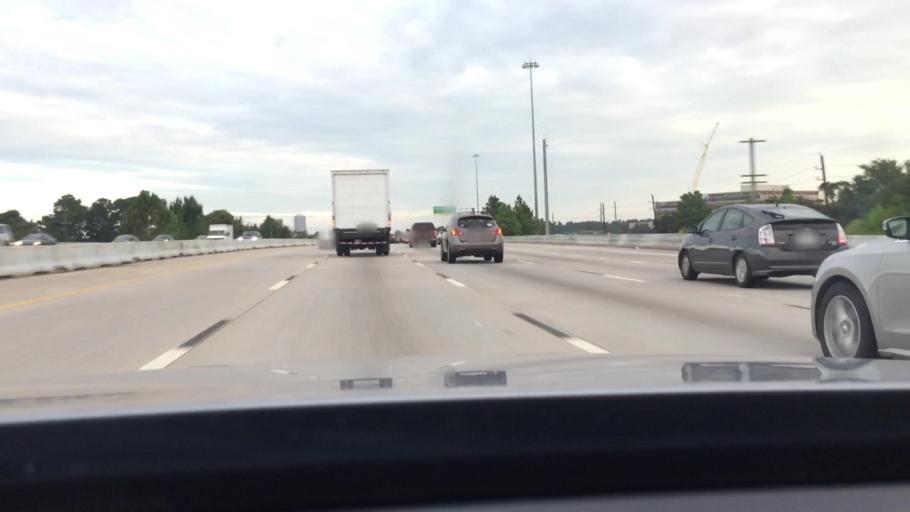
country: US
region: Texas
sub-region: Harris County
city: Oak Cliff Place
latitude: 29.9731
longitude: -95.5631
